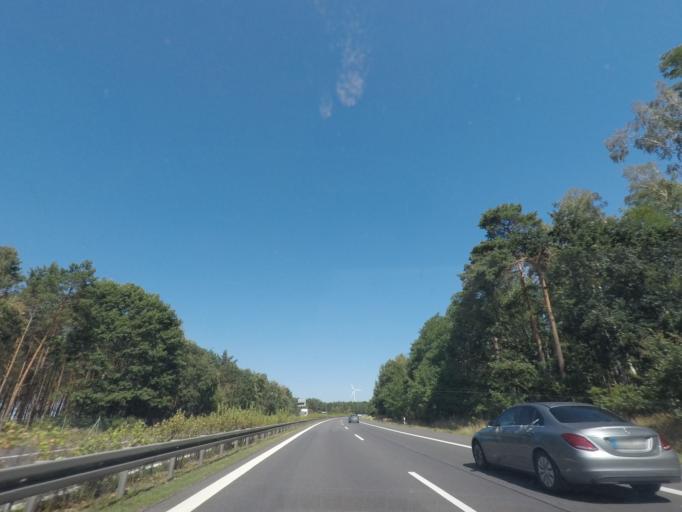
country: DE
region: Brandenburg
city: Bronkow
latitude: 51.6706
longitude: 13.9030
